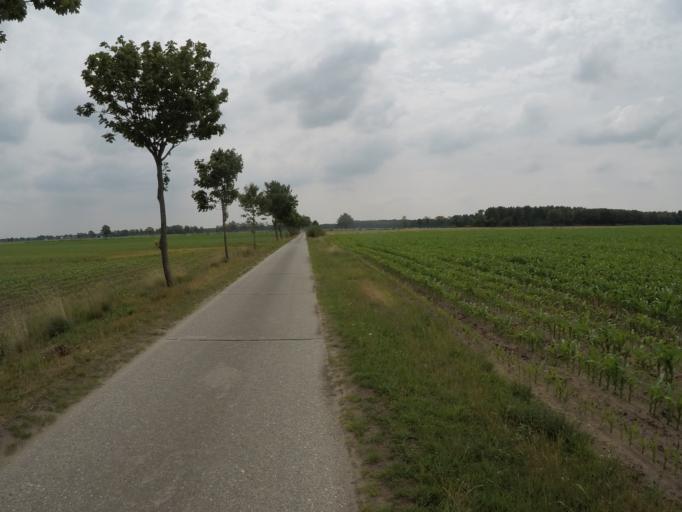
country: BE
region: Flanders
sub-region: Provincie Antwerpen
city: Wuustwezel
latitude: 51.4269
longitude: 4.5713
